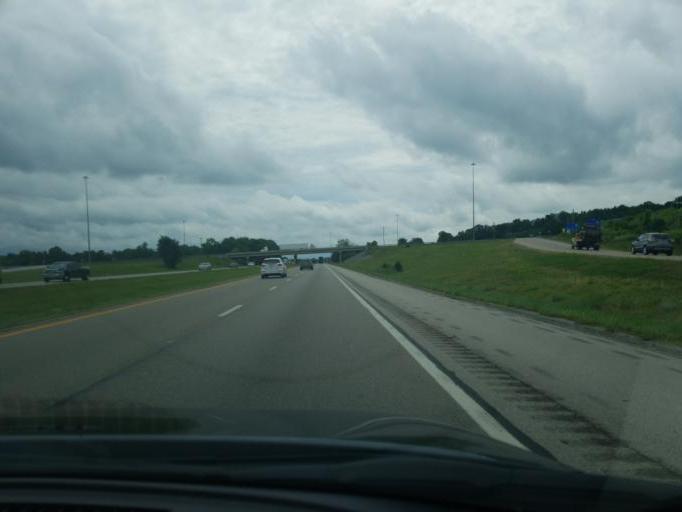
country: US
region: Kentucky
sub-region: Gallatin County
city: Warsaw
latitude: 38.6929
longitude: -84.9355
